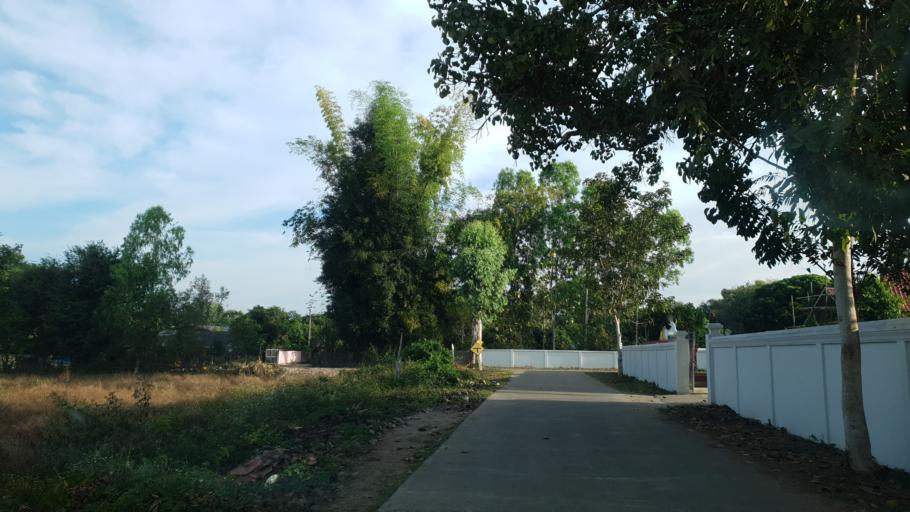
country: TH
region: Lamphun
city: Lamphun
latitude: 18.5131
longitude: 99.0268
